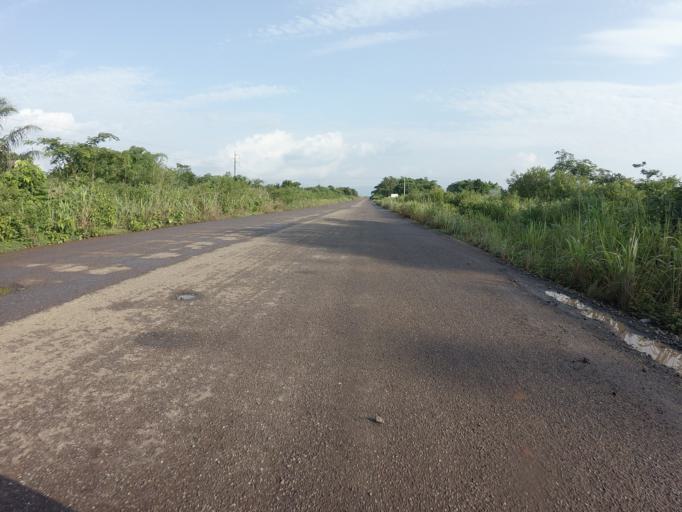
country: GH
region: Volta
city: Hohoe
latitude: 7.0239
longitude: 0.4278
